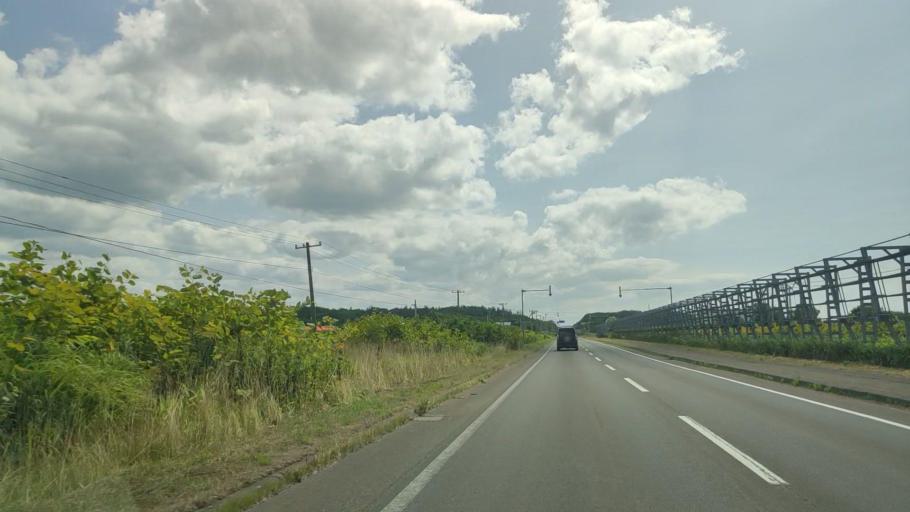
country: JP
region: Hokkaido
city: Makubetsu
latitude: 44.7725
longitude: 141.7922
